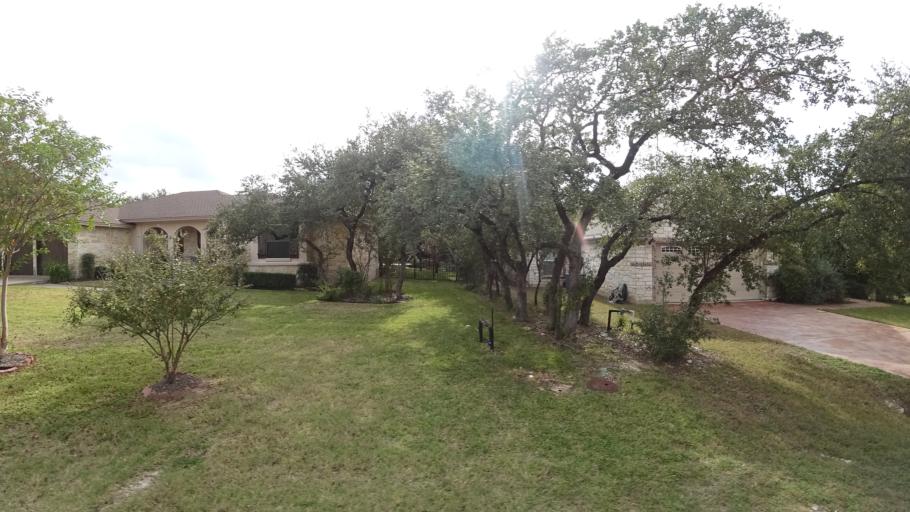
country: US
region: Texas
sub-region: Travis County
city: Hudson Bend
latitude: 30.3812
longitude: -97.9052
